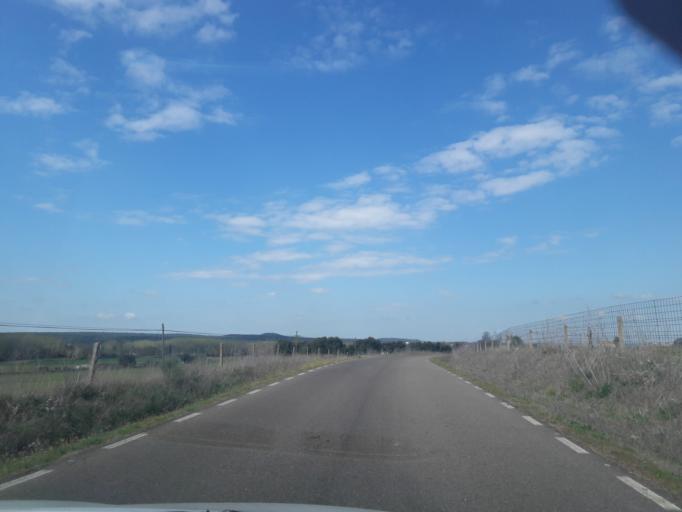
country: ES
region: Castille and Leon
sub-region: Provincia de Salamanca
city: Zamarra
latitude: 40.5675
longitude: -6.4801
